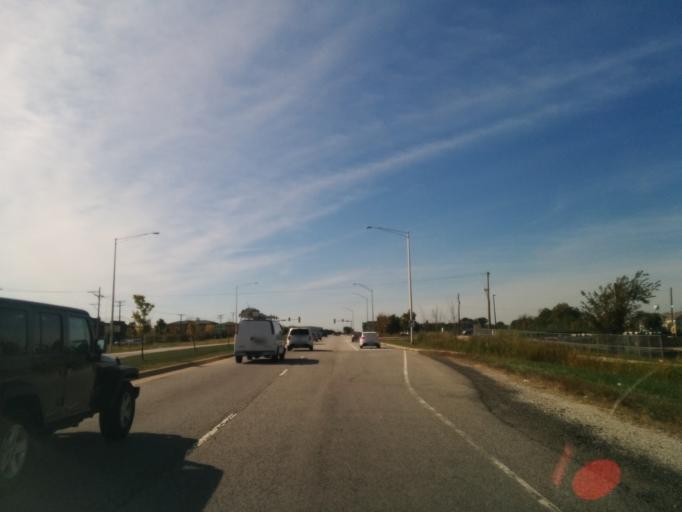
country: US
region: Illinois
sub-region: Kane County
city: North Aurora
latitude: 41.8131
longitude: -88.2808
